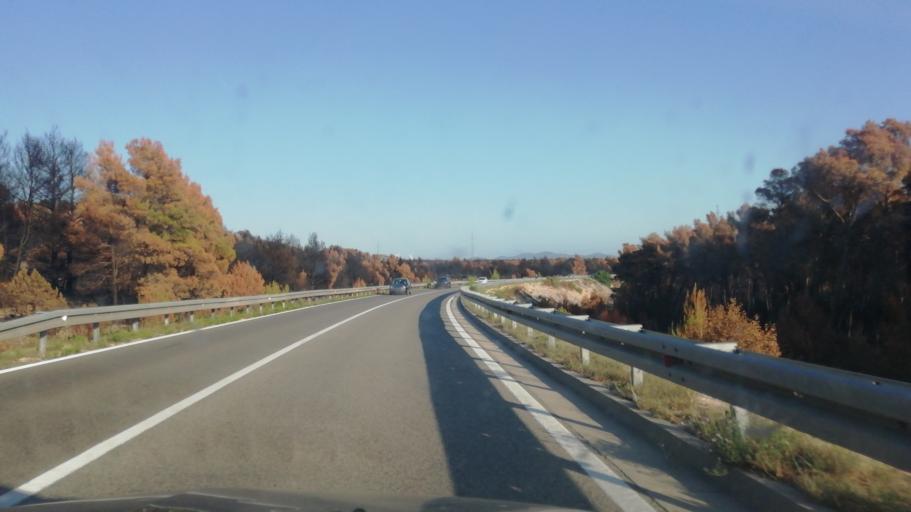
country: HR
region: Sibensko-Kniniska
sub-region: Grad Sibenik
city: Sibenik
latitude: 43.7500
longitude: 15.9408
